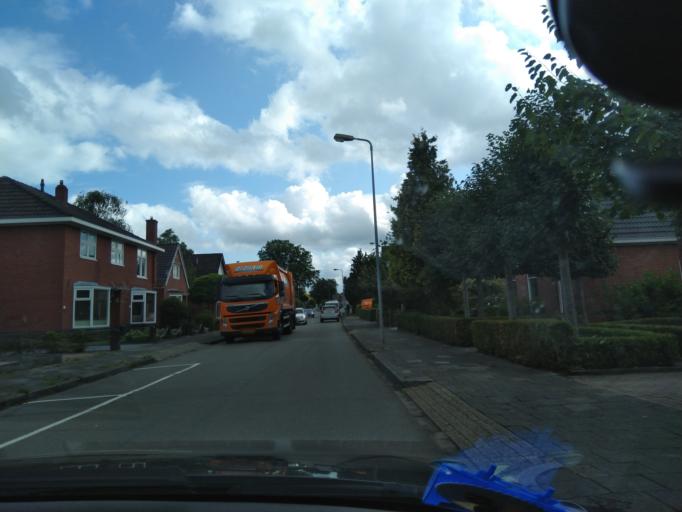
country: NL
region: Groningen
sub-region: Gemeente Zuidhorn
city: Aduard
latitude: 53.2209
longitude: 6.5003
